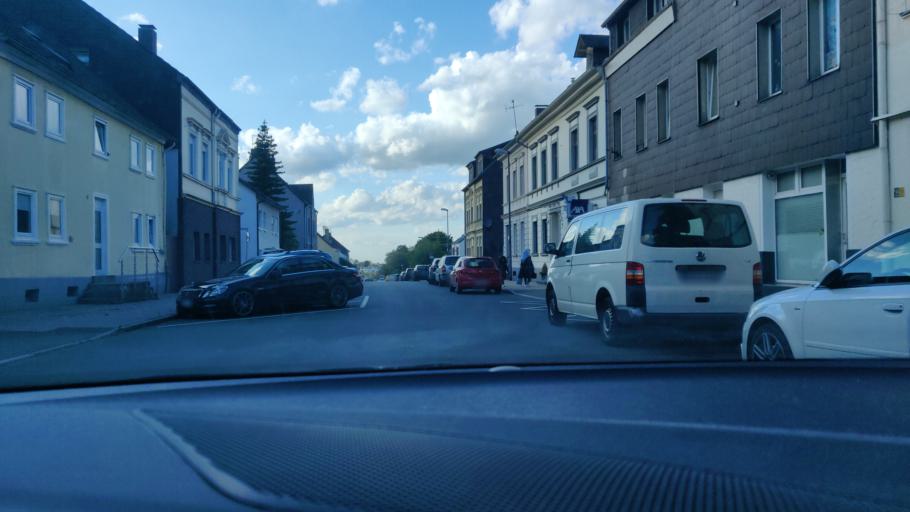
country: DE
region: North Rhine-Westphalia
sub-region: Regierungsbezirk Dusseldorf
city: Velbert
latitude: 51.3450
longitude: 7.0331
